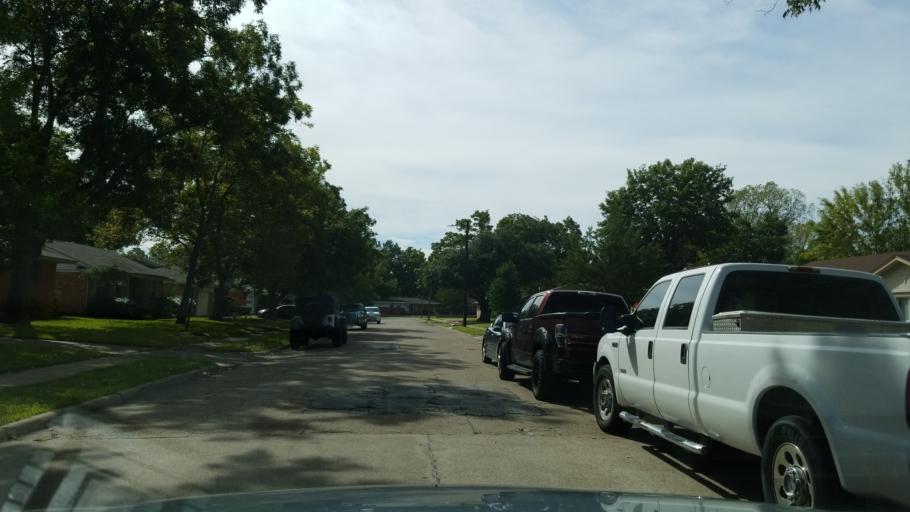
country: US
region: Texas
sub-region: Dallas County
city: Garland
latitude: 32.9010
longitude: -96.6599
